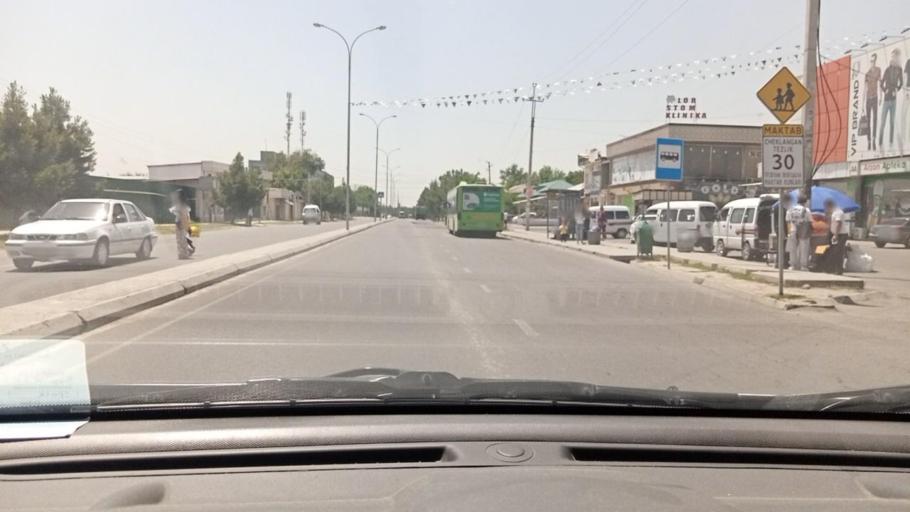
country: UZ
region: Toshkent
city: Urtaowul
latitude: 41.2264
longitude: 69.1795
